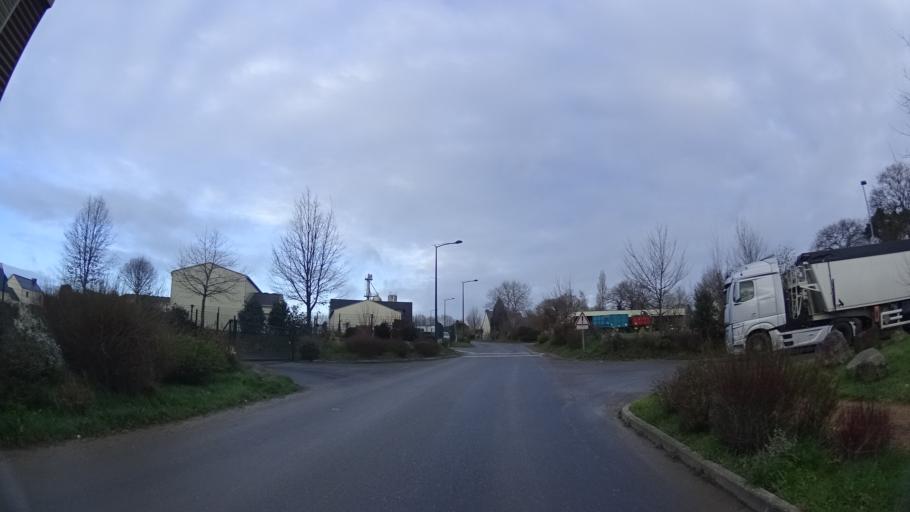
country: FR
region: Brittany
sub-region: Departement d'Ille-et-Vilaine
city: Romille
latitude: 48.2195
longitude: -1.8892
